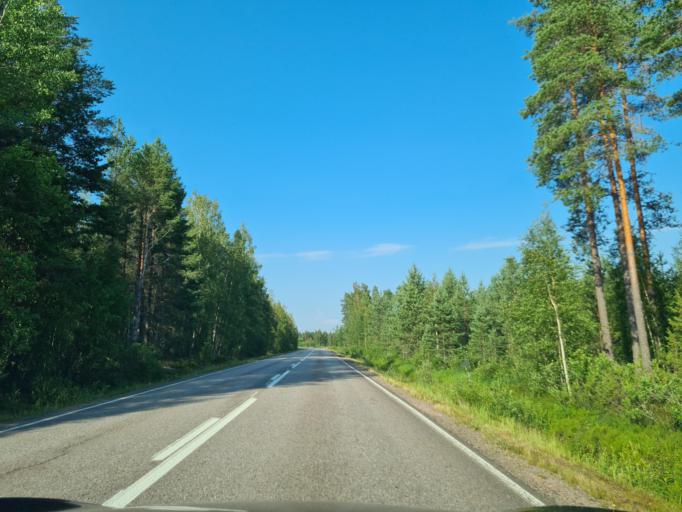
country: FI
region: Satakunta
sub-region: Pohjois-Satakunta
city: Karvia
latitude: 62.3101
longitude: 22.6516
